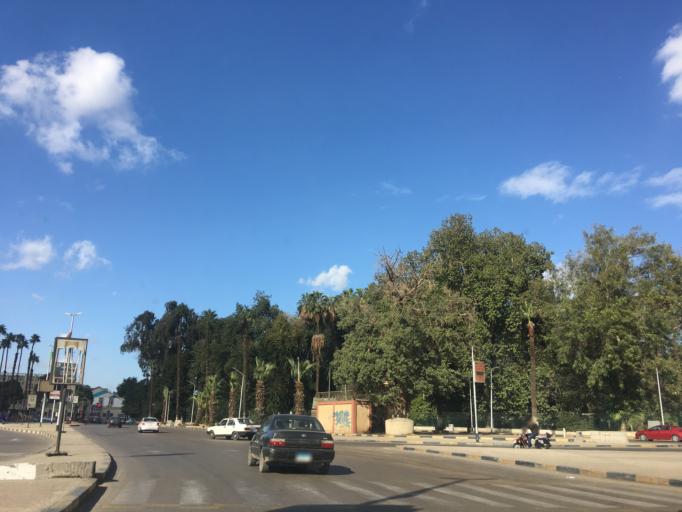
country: EG
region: Al Jizah
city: Al Jizah
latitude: 30.0276
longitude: 31.2110
